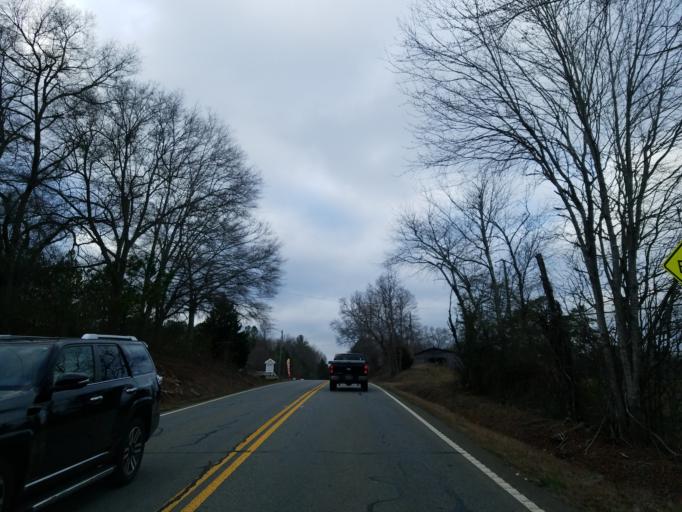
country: US
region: Georgia
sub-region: Cherokee County
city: Canton
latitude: 34.3058
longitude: -84.5277
